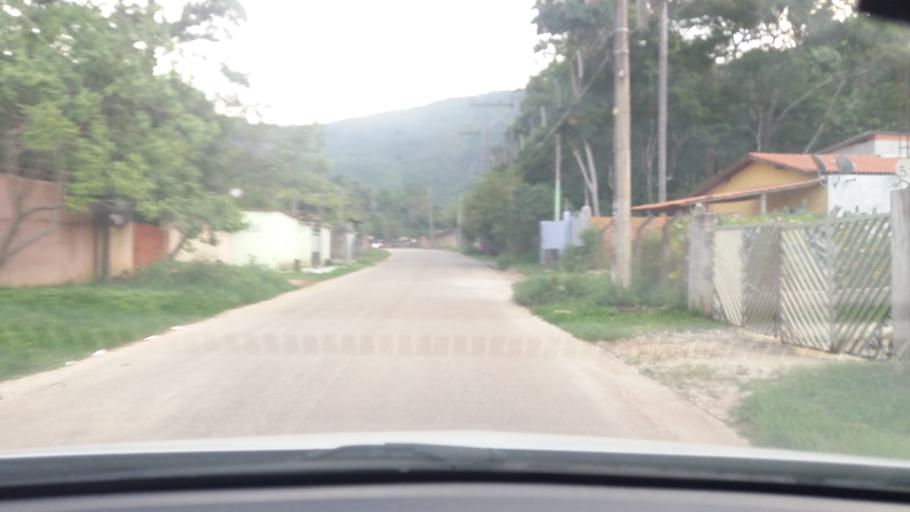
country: BR
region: Sao Paulo
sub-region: Bom Jesus Dos Perdoes
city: Bom Jesus dos Perdoes
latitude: -23.1777
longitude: -46.4848
